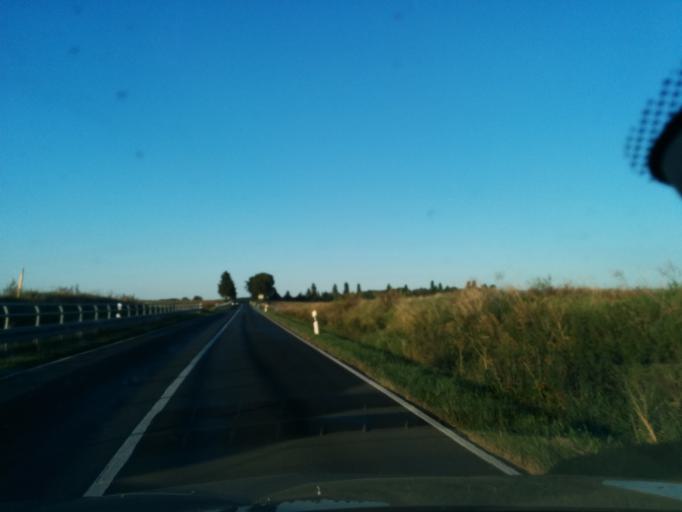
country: DE
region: Mecklenburg-Vorpommern
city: Loddin
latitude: 53.9214
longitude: 14.0220
